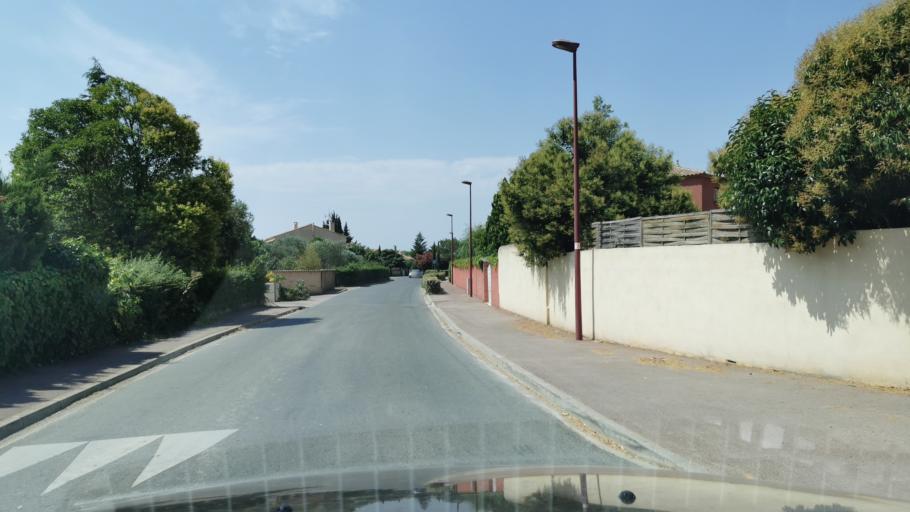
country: FR
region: Languedoc-Roussillon
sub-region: Departement de l'Aude
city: Argeliers
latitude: 43.2826
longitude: 2.8984
